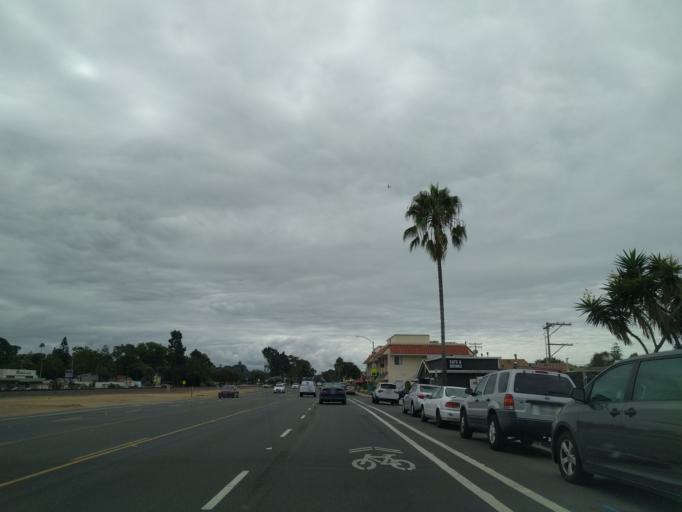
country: US
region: California
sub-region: San Diego County
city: Encinitas
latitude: 33.0601
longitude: -117.3005
